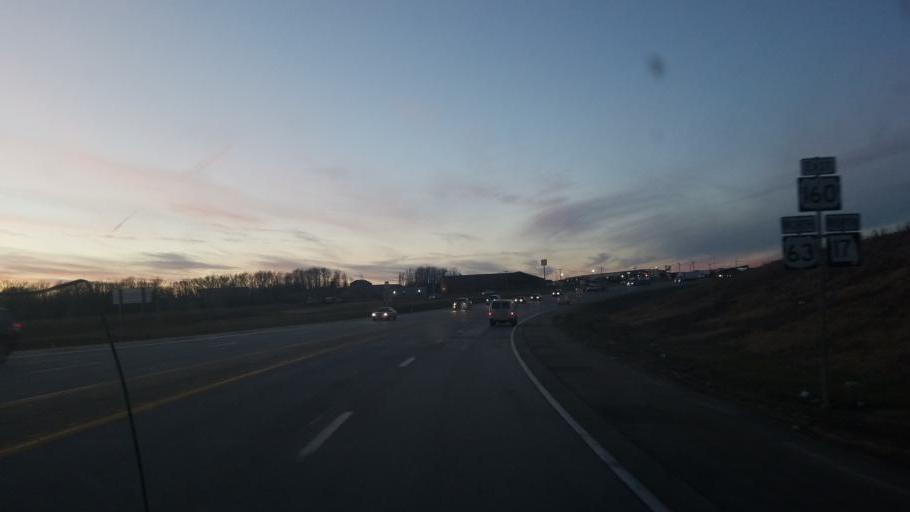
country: US
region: Missouri
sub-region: Howell County
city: West Plains
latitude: 36.7185
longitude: -91.8741
